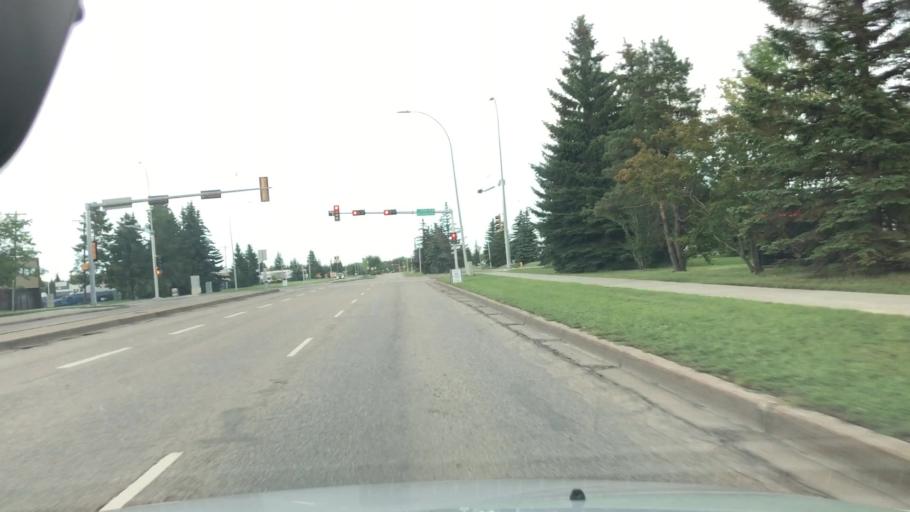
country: CA
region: Alberta
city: St. Albert
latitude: 53.6360
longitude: -113.5758
